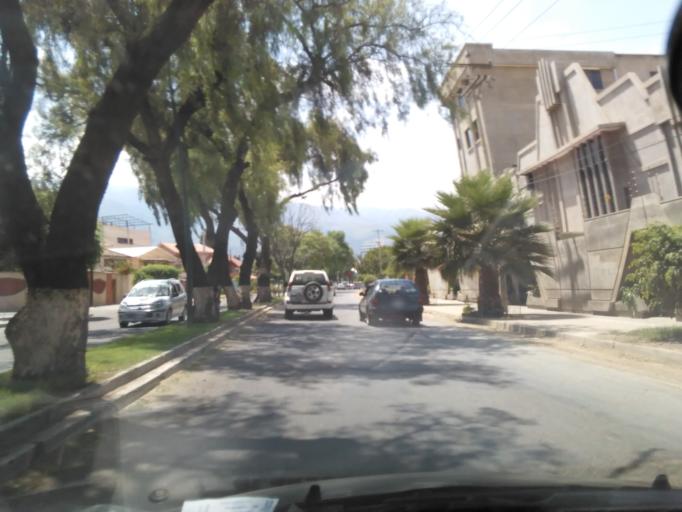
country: BO
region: Cochabamba
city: Cochabamba
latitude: -17.3831
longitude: -66.1635
